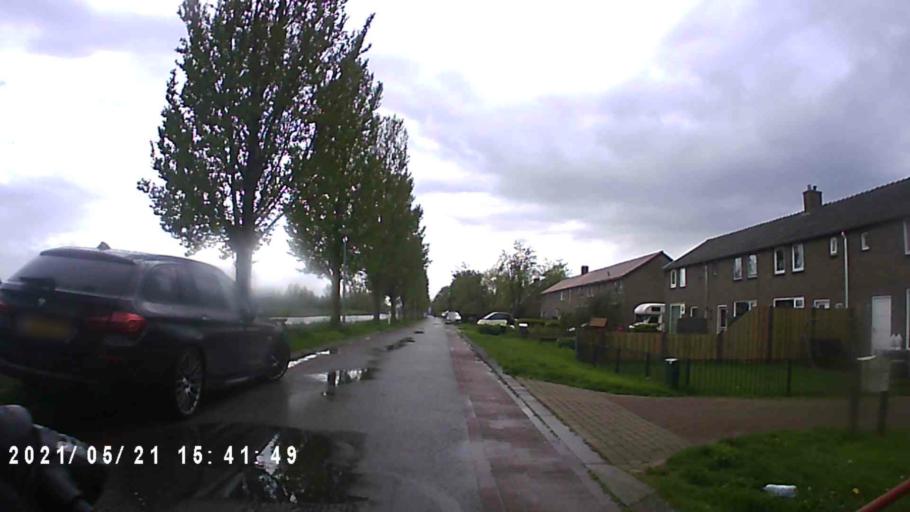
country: NL
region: Groningen
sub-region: Gemeente Zuidhorn
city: Aduard
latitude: 53.2024
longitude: 6.4495
